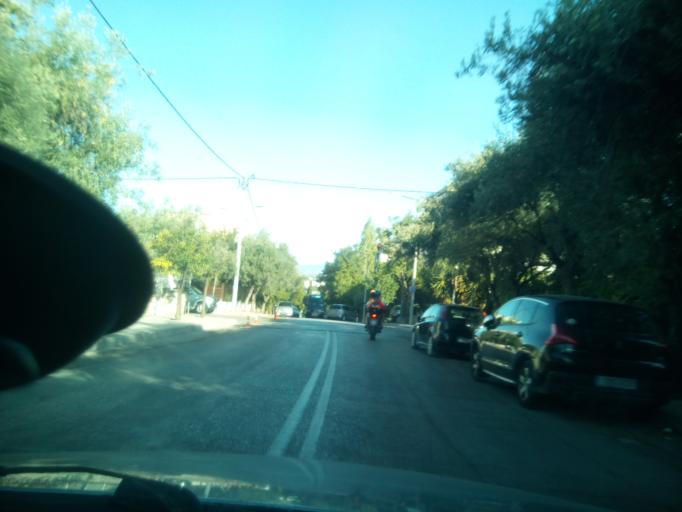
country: GR
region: Attica
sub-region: Nomarchia Athinas
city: Papagou
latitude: 37.9904
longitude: 23.7934
